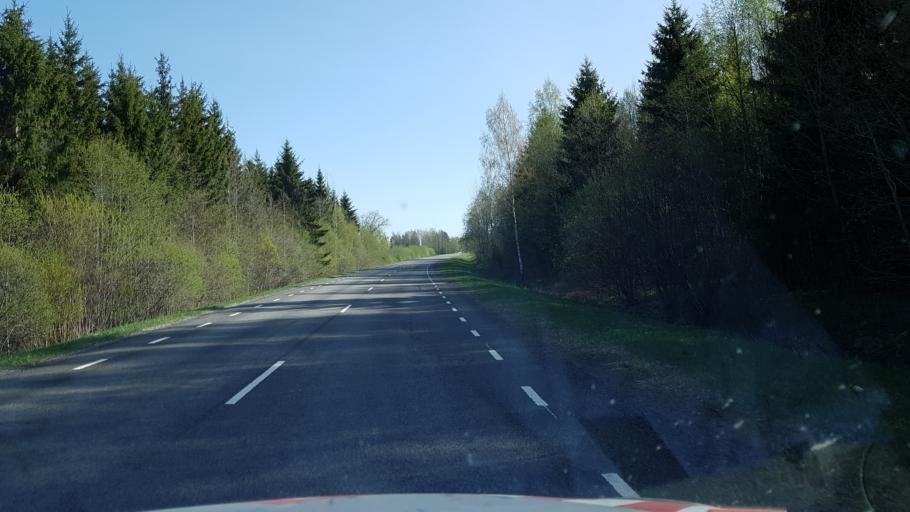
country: EE
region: Viljandimaa
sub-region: Karksi vald
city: Karksi-Nuia
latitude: 58.2088
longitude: 25.5396
